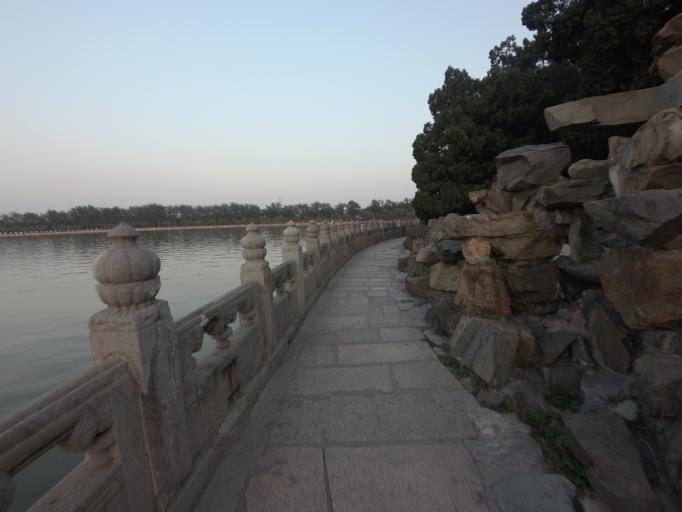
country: CN
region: Beijing
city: Haidian
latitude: 39.9906
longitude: 116.2703
